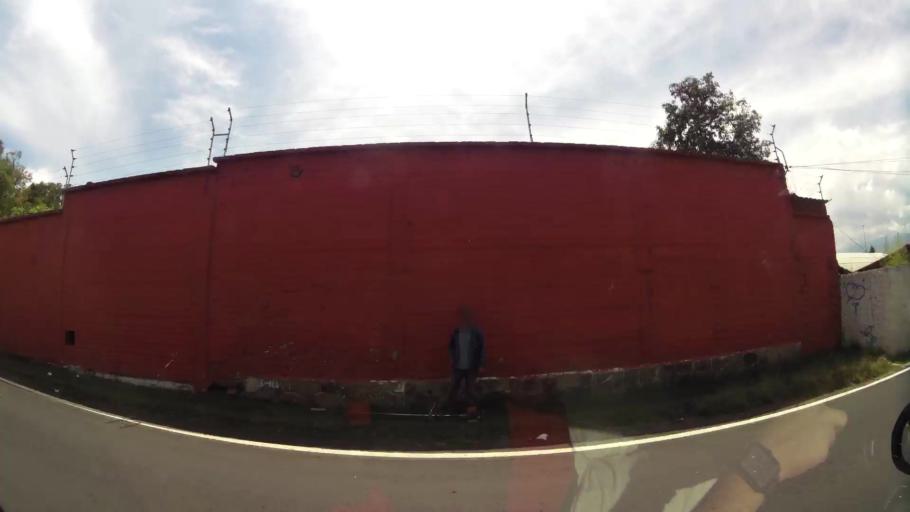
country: EC
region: Pichincha
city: Quito
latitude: -0.2096
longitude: -78.4111
